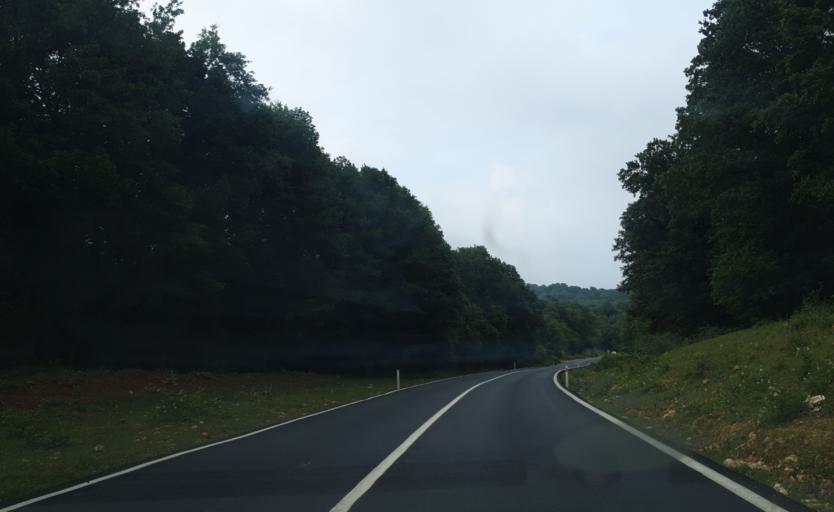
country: TR
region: Kirklareli
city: Salmydessus
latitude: 41.6064
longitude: 28.0843
